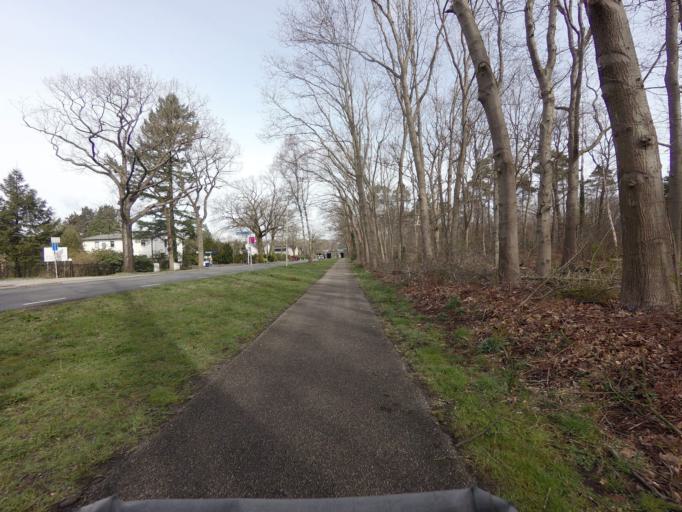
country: NL
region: Gelderland
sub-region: Gemeente Arnhem
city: Hoogkamp
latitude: 52.0241
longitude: 5.8726
